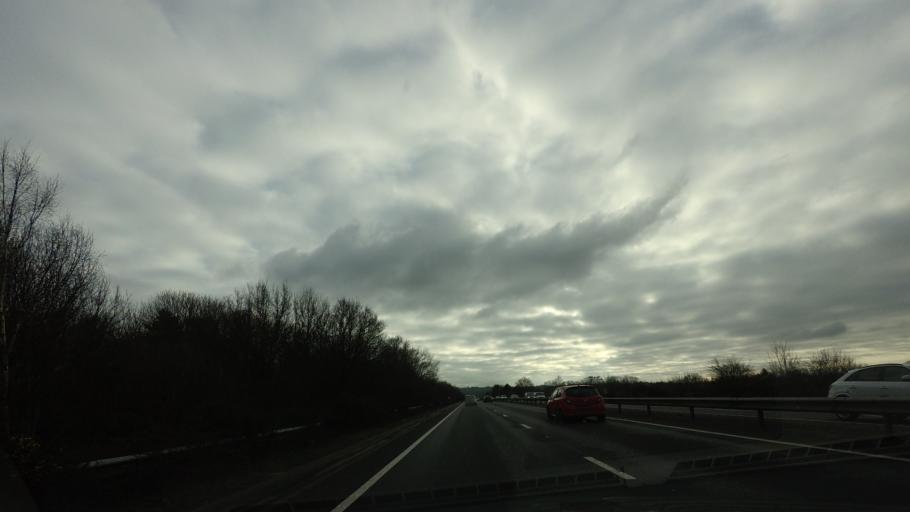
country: GB
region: England
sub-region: Kent
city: Tonbridge
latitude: 51.1975
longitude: 0.2316
